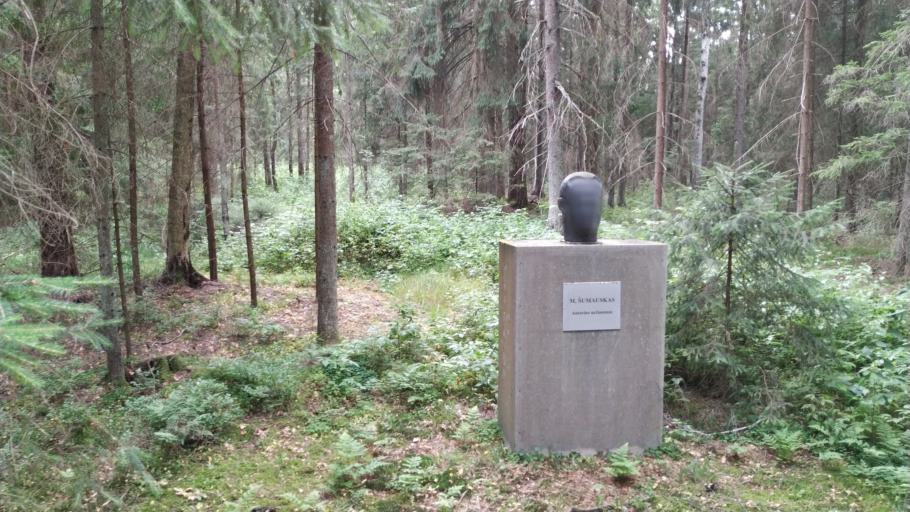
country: LT
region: Alytaus apskritis
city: Druskininkai
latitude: 54.0204
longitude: 24.0817
